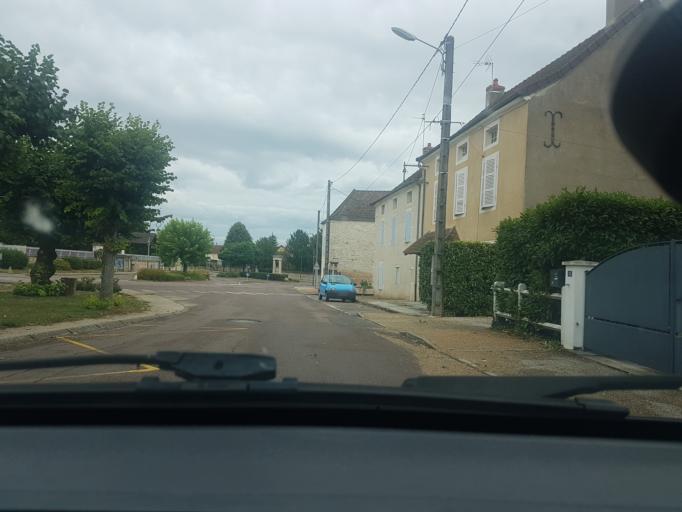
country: FR
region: Bourgogne
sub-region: Departement de Saone-et-Loire
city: Fontaines
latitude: 46.8517
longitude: 4.7699
